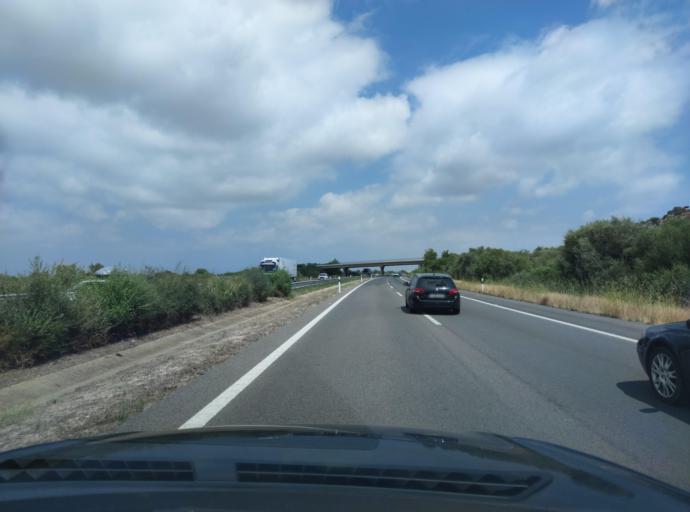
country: ES
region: Valencia
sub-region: Provincia de Castello
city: Vinaros
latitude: 40.4885
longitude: 0.4153
